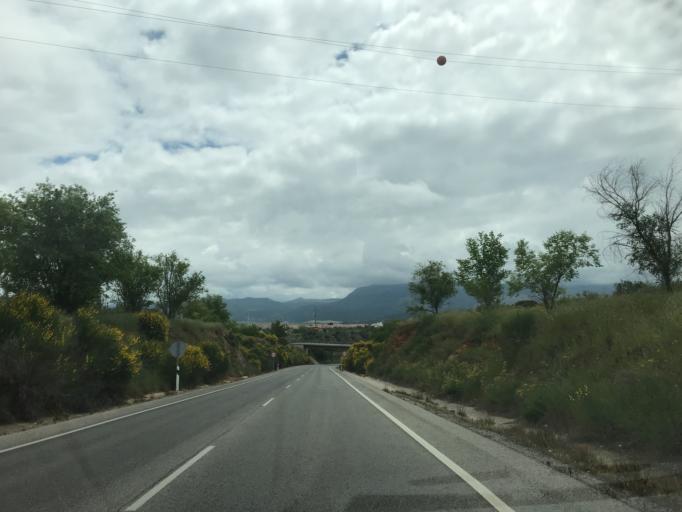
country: ES
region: Andalusia
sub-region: Provincia de Malaga
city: Ronda
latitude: 36.7252
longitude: -5.1674
